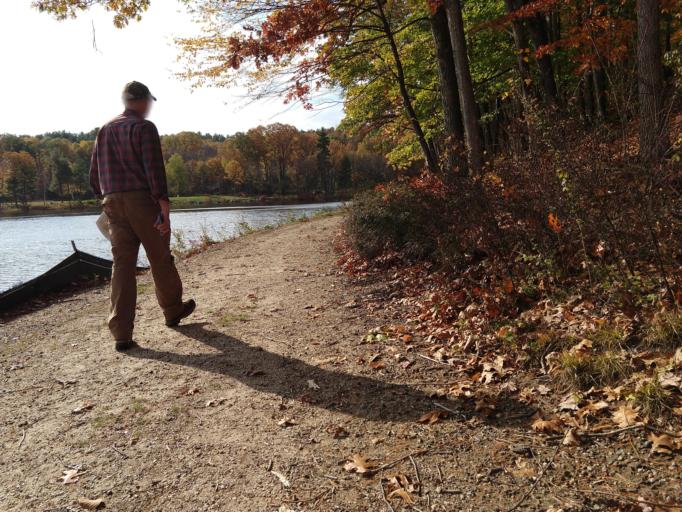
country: US
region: Massachusetts
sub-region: Worcester County
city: Leominster
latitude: 42.5219
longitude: -71.7738
